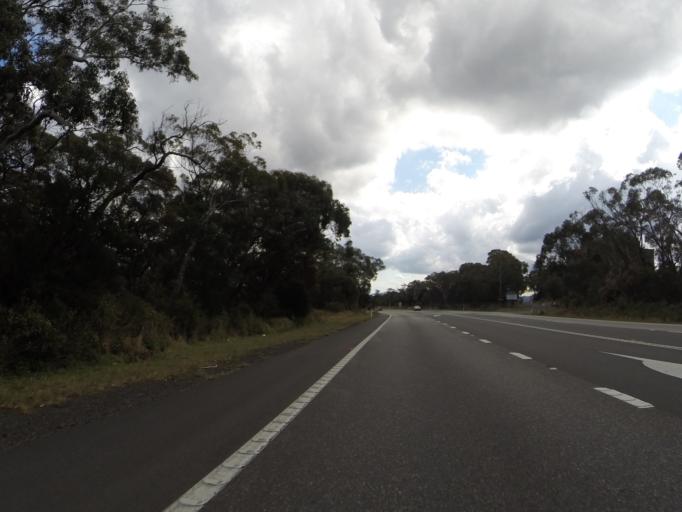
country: AU
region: New South Wales
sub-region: Wollongong
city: Mount Keira
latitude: -34.3439
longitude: 150.7965
